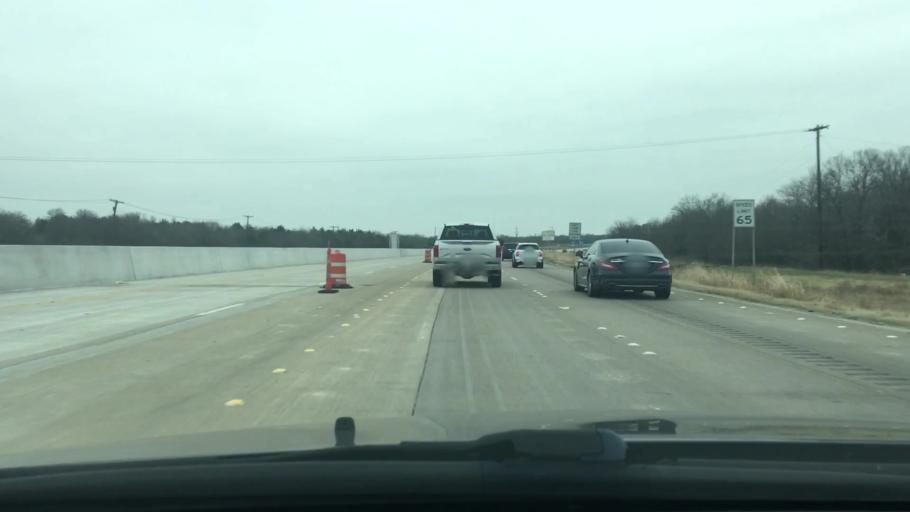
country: US
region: Texas
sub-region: Navarro County
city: Corsicana
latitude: 32.0876
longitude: -96.4391
